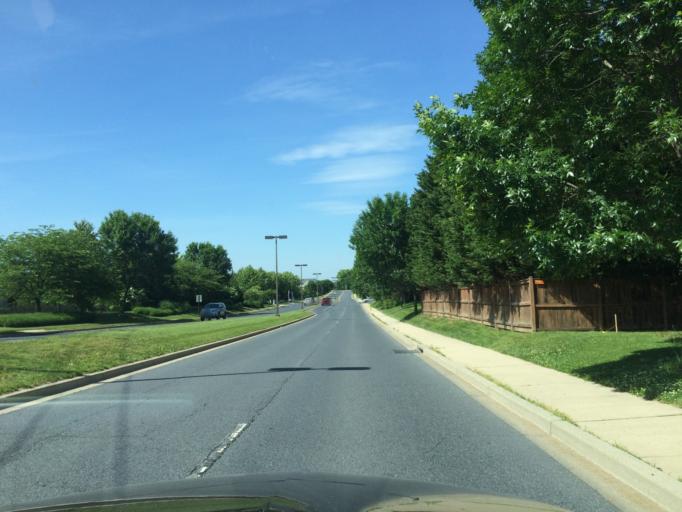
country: US
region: Maryland
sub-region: Frederick County
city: Clover Hill
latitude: 39.4603
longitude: -77.4161
